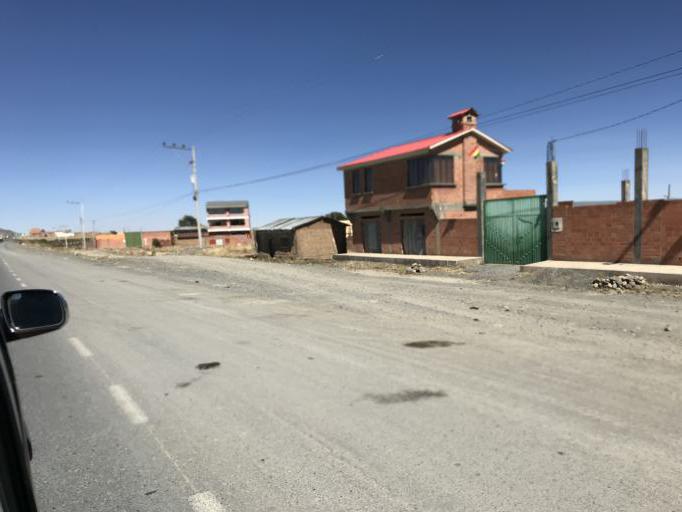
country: BO
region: La Paz
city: Batallas
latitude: -16.3277
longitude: -68.4247
